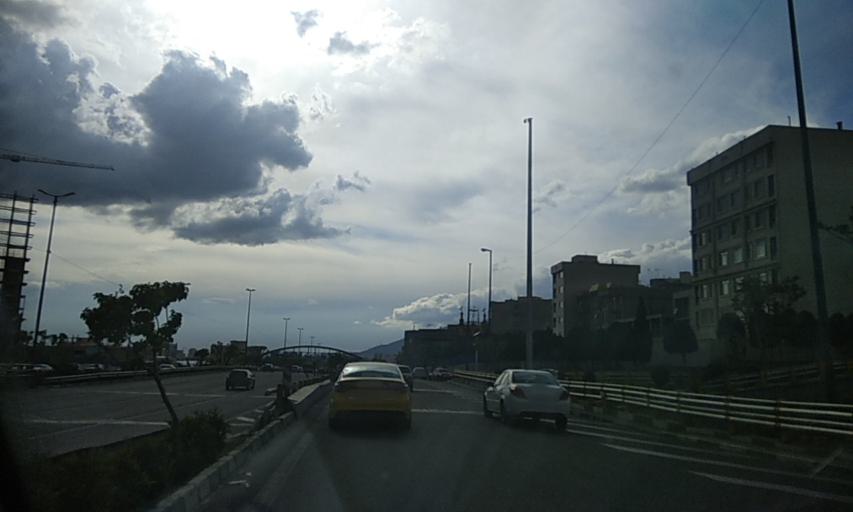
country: IR
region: Tehran
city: Tehran
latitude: 35.7537
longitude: 51.2897
